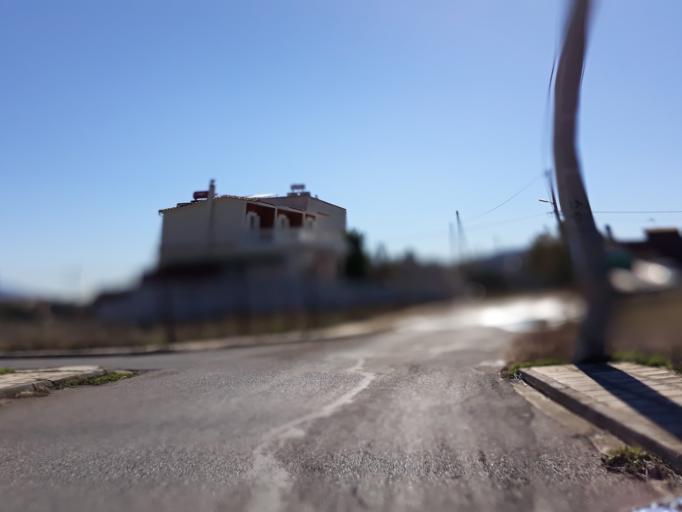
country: GR
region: Attica
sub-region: Nomarchia Dytikis Attikis
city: Ano Liosia
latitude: 38.0922
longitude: 23.7094
